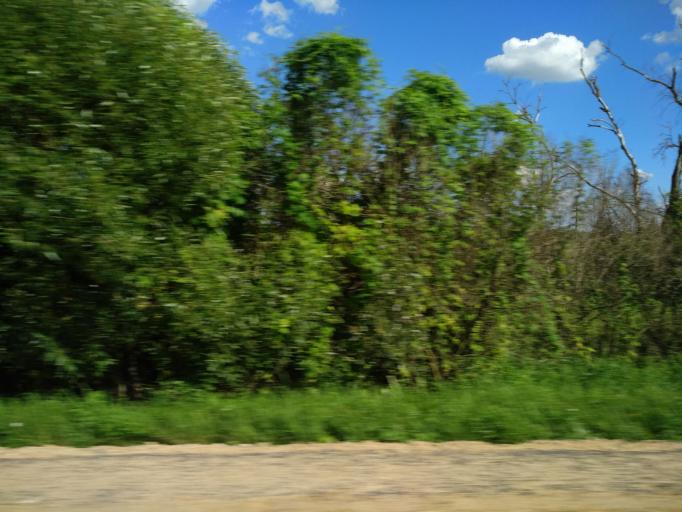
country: BY
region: Vitebsk
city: Mosar
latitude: 55.1015
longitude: 27.1995
